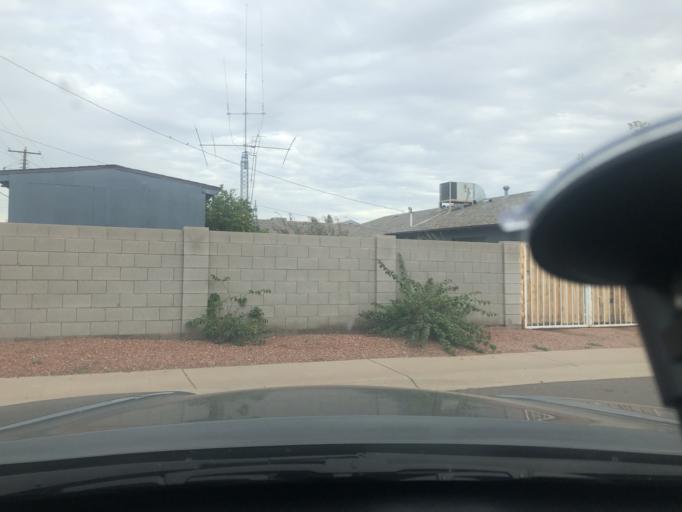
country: US
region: Arizona
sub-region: Maricopa County
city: Scottsdale
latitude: 33.4770
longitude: -111.8961
